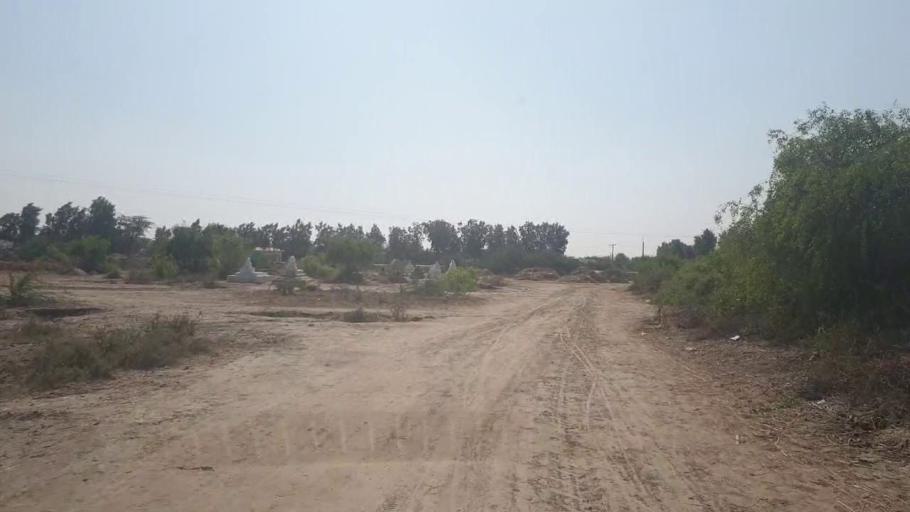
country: PK
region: Sindh
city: Badin
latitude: 24.6780
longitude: 68.9008
